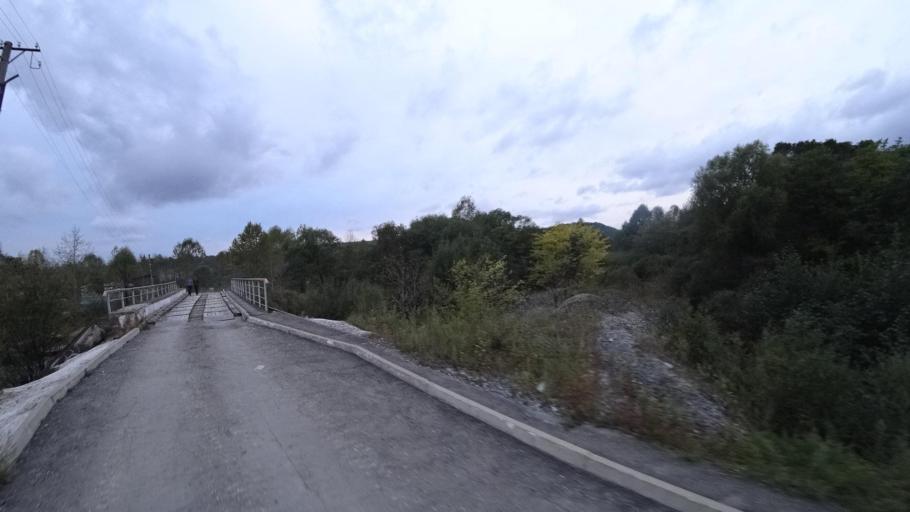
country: RU
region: Jewish Autonomous Oblast
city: Izvestkovyy
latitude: 48.9910
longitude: 131.5555
